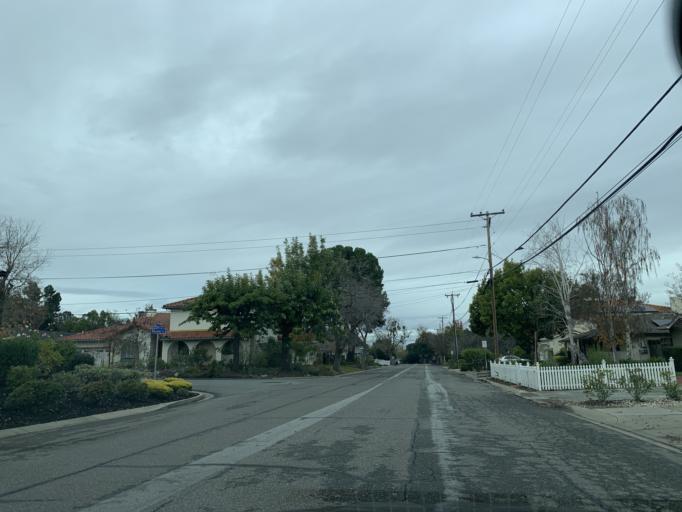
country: US
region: California
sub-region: Santa Clara County
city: Cupertino
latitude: 37.3254
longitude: -122.0561
